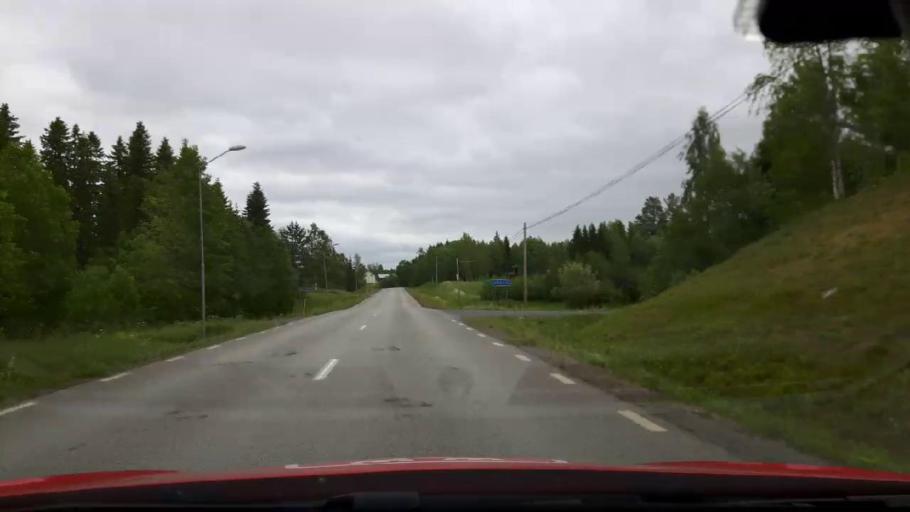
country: SE
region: Jaemtland
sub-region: OEstersunds Kommun
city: Lit
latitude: 63.6766
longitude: 15.0526
